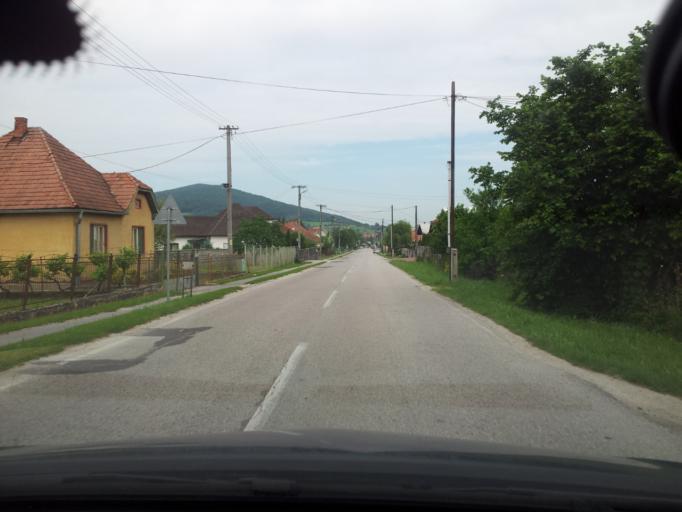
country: SK
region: Nitriansky
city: Partizanske
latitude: 48.6017
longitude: 18.4452
